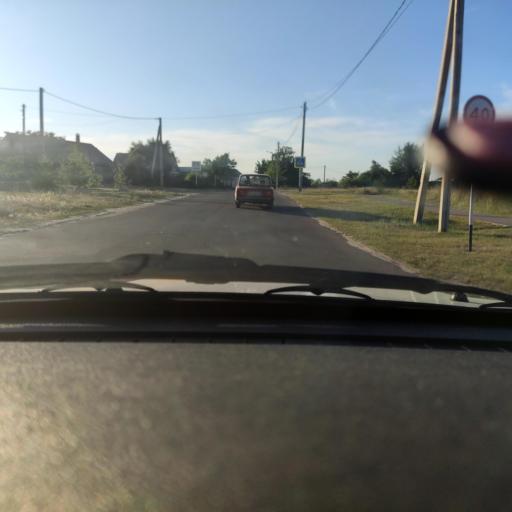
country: RU
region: Voronezj
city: Ramon'
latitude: 51.9010
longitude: 39.2863
